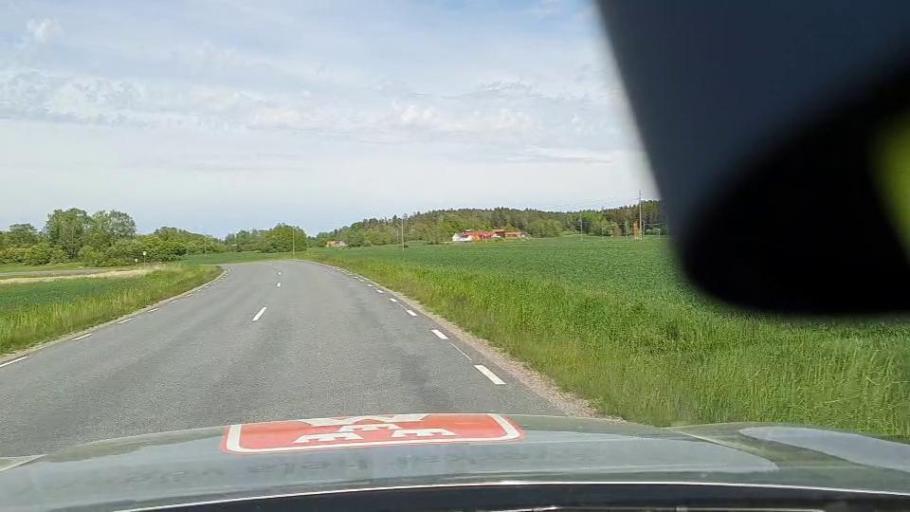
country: SE
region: Soedermanland
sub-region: Eskilstuna Kommun
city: Skogstorp
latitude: 59.3110
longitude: 16.4643
